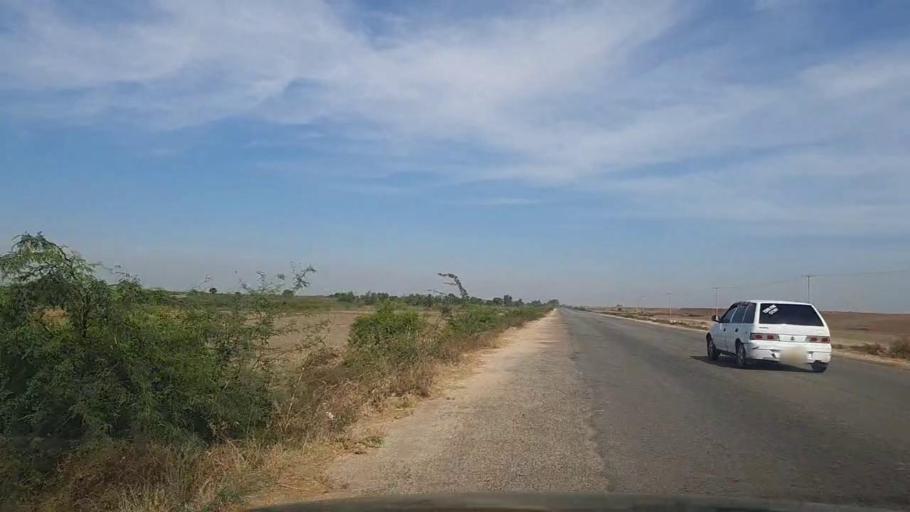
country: PK
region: Sindh
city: Daro Mehar
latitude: 24.9455
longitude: 68.1111
